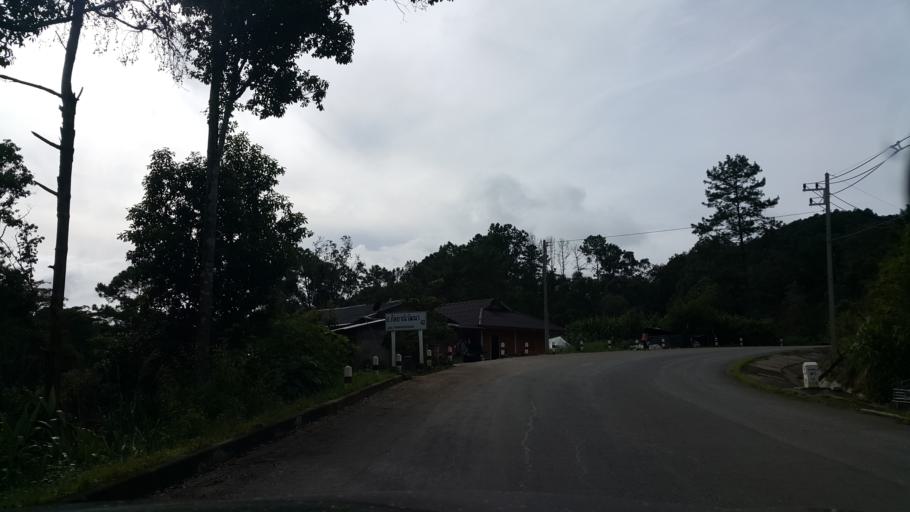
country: TH
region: Chiang Mai
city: Chaem Luang
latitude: 18.9372
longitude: 98.4640
